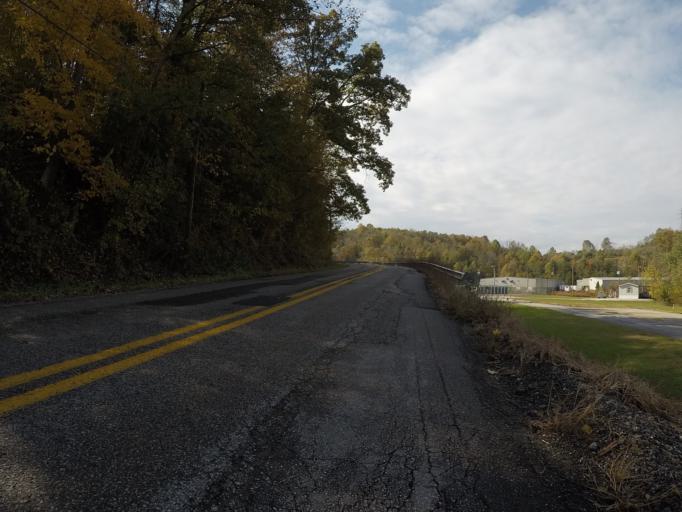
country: US
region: West Virginia
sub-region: Cabell County
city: Huntington
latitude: 38.3858
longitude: -82.3940
